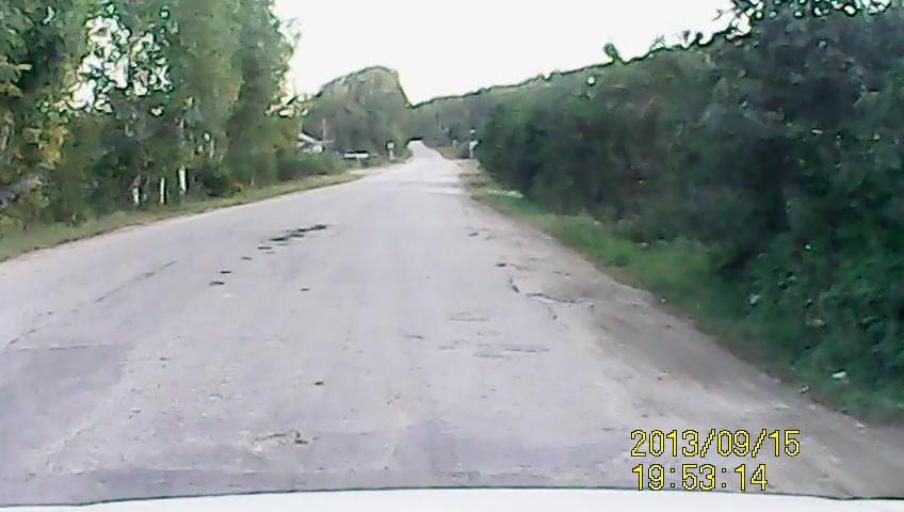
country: RU
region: Chelyabinsk
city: Kyshtym
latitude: 55.7649
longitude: 60.4857
